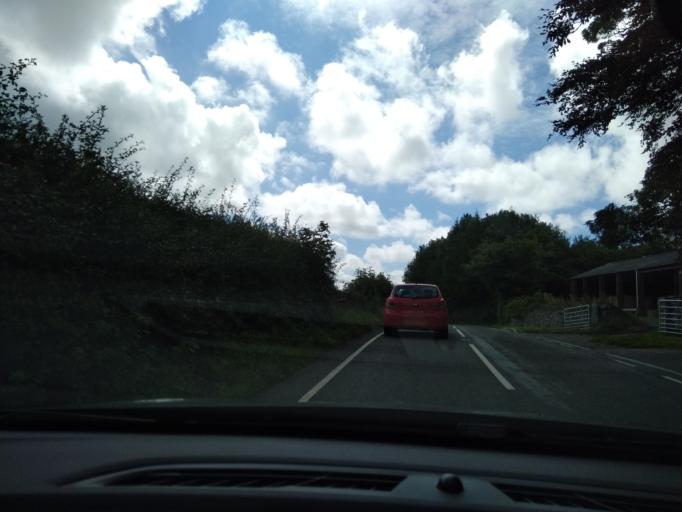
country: GB
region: England
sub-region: Cumbria
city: Millom
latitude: 54.2497
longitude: -3.3052
